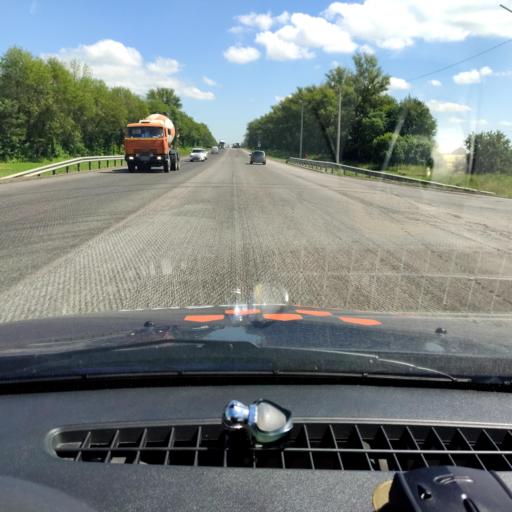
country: RU
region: Orjol
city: Zmiyevka
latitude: 52.7100
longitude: 36.3548
